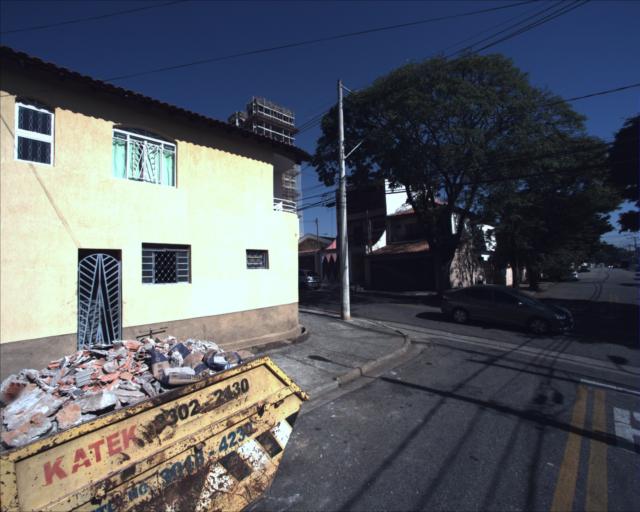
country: BR
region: Sao Paulo
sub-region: Sorocaba
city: Sorocaba
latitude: -23.5046
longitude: -47.4420
